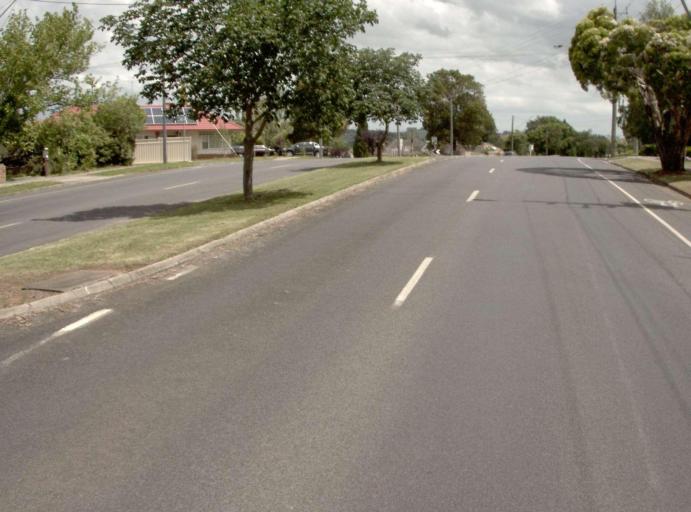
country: AU
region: Victoria
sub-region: Baw Baw
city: Warragul
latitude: -38.1542
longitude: 145.9341
